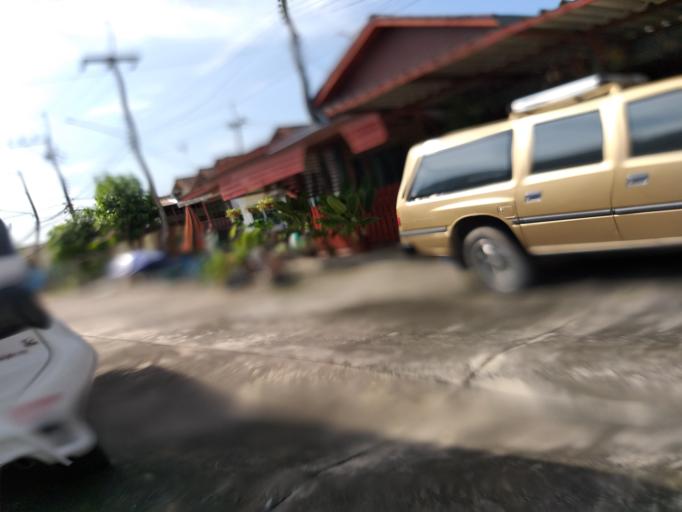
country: TH
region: Pathum Thani
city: Nong Suea
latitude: 14.0560
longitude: 100.8549
